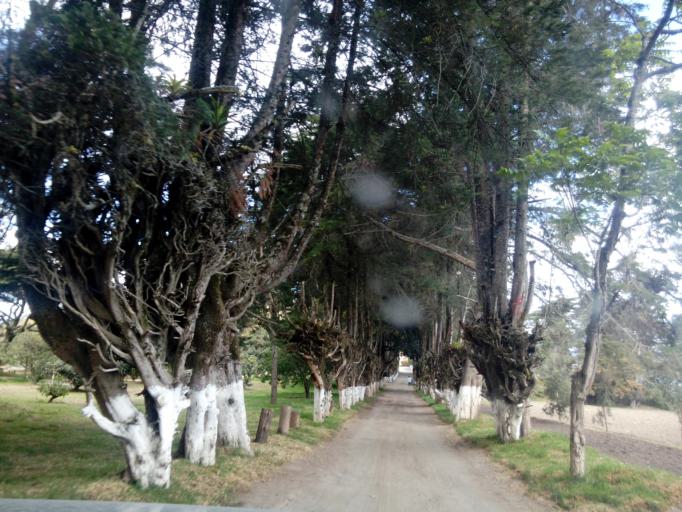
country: EC
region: Imbabura
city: Atuntaqui
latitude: 0.4184
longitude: -78.1895
